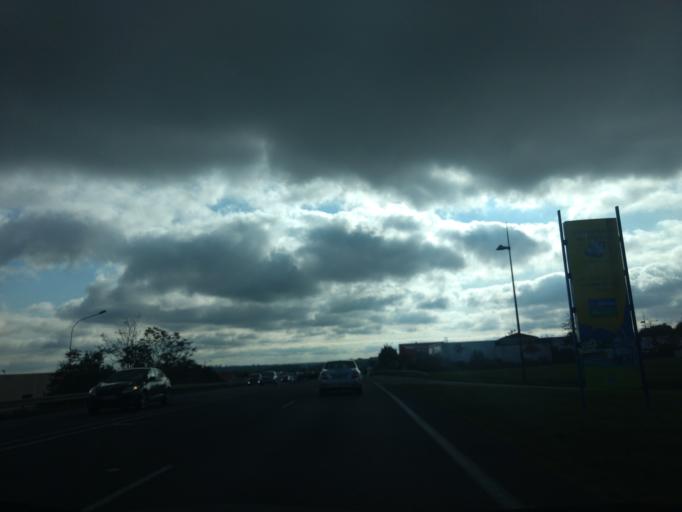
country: FR
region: Poitou-Charentes
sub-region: Departement de la Vienne
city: Chasseneuil-du-Poitou
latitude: 46.6546
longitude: 0.3657
